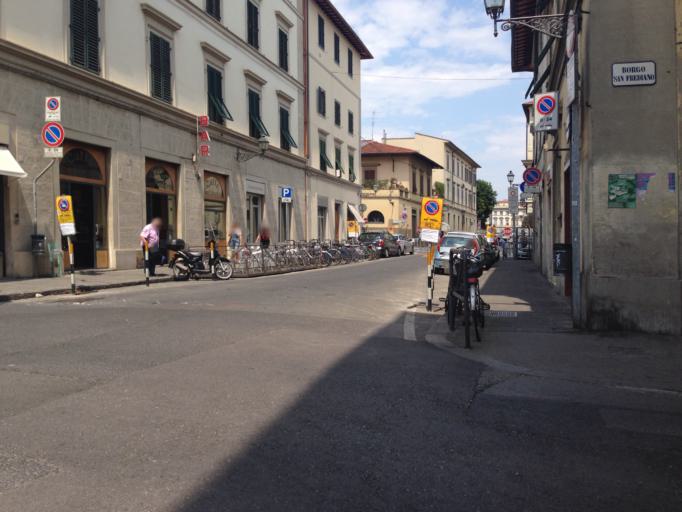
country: IT
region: Tuscany
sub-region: Province of Florence
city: Florence
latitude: 43.7701
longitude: 11.2418
